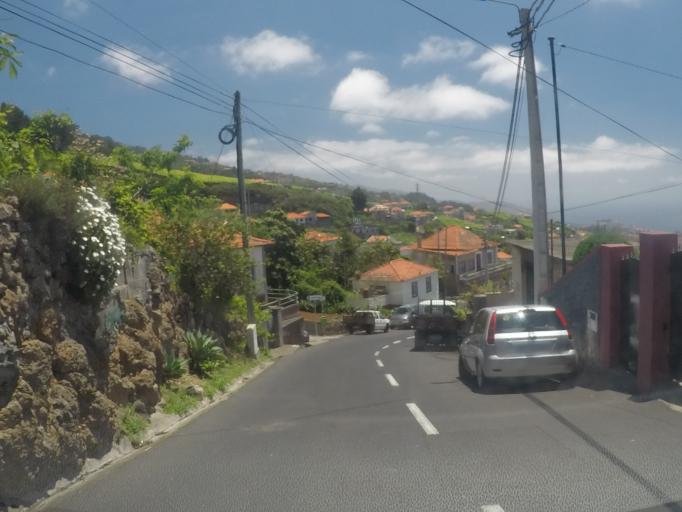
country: PT
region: Madeira
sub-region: Camara de Lobos
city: Curral das Freiras
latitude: 32.6808
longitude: -16.9906
